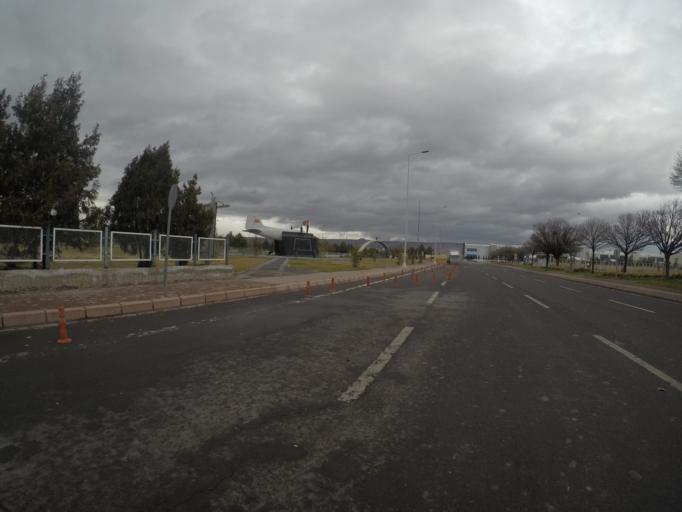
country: TR
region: Kayseri
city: Kayseri
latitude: 38.7630
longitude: 35.4816
